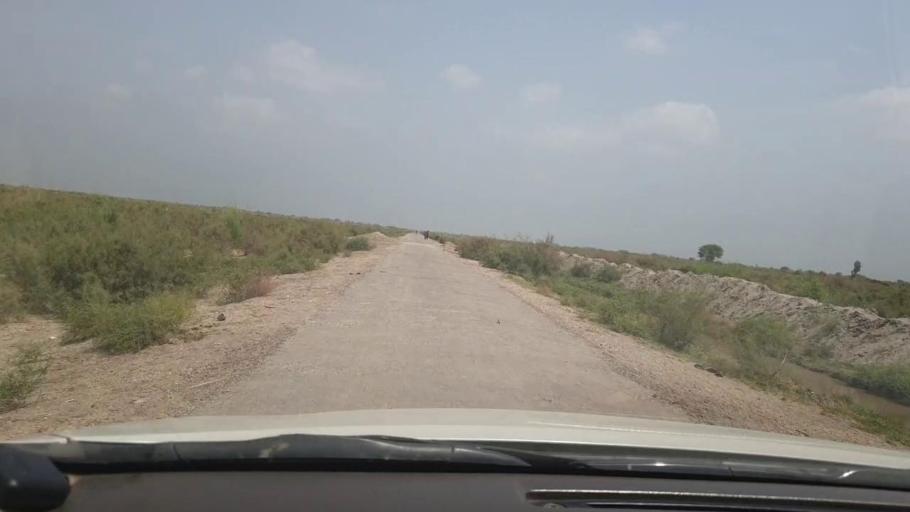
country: PK
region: Sindh
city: Garhi Yasin
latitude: 28.0182
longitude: 68.5000
